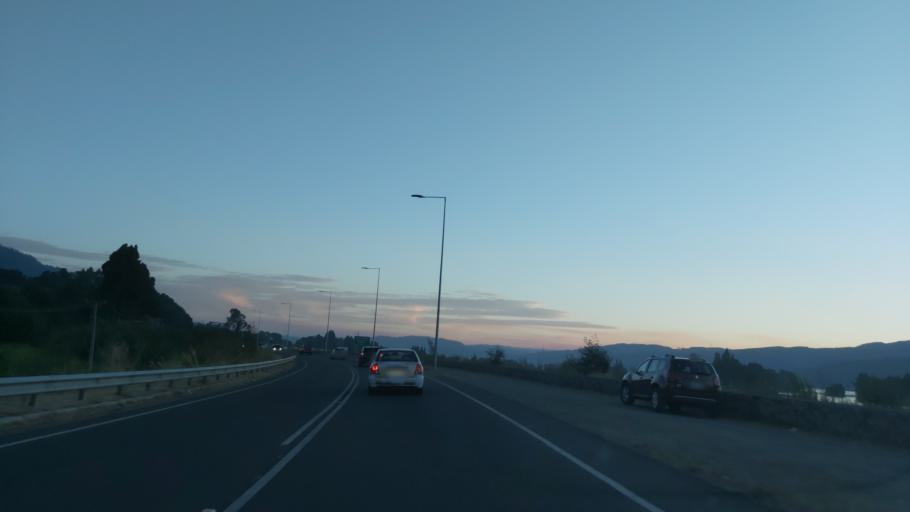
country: CL
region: Biobio
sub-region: Provincia de Concepcion
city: Chiguayante
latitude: -36.8872
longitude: -73.0382
